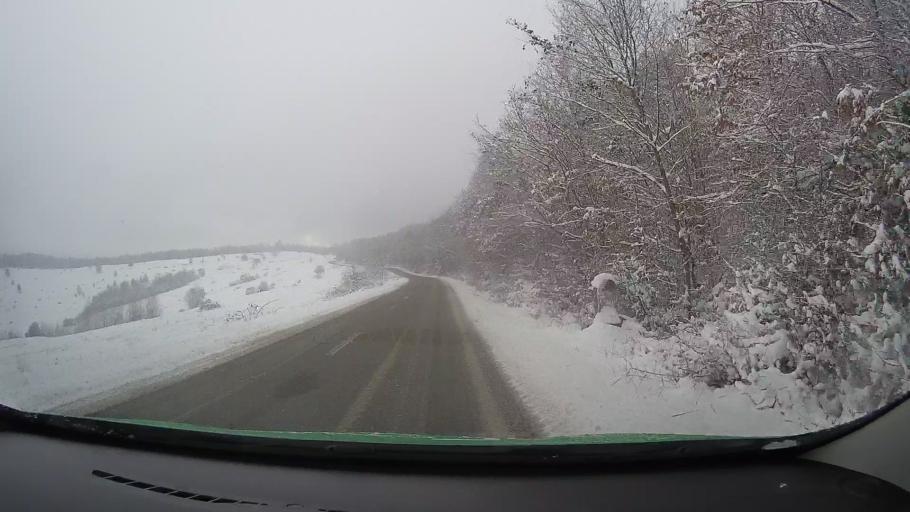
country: RO
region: Hunedoara
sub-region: Comuna Teliucu Inferior
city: Teliucu Inferior
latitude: 45.6858
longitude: 22.9092
